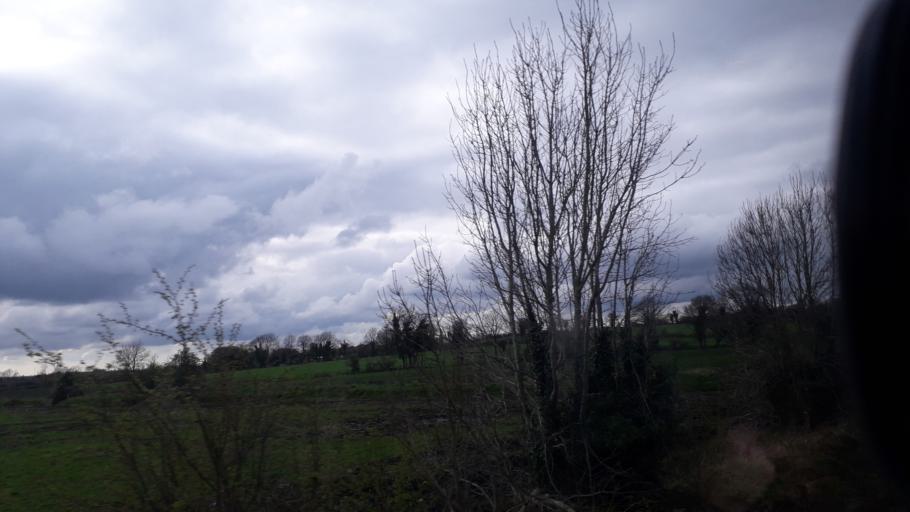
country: IE
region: Leinster
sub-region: An Longfort
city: Longford
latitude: 53.7262
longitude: -7.8162
